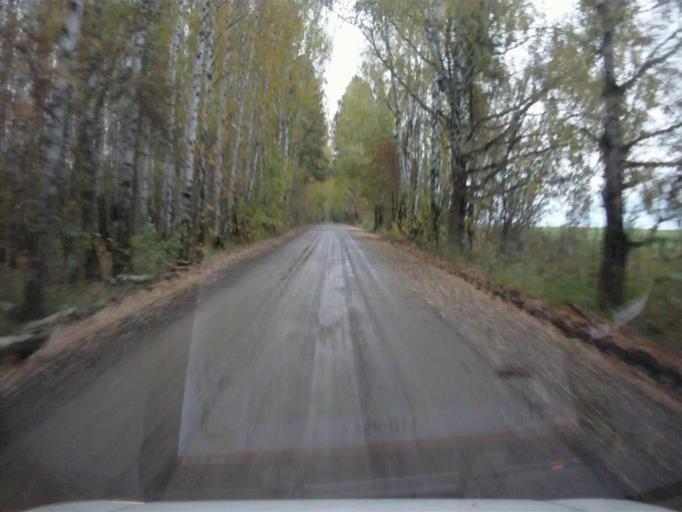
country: RU
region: Sverdlovsk
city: Mikhaylovsk
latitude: 56.1708
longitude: 59.2228
